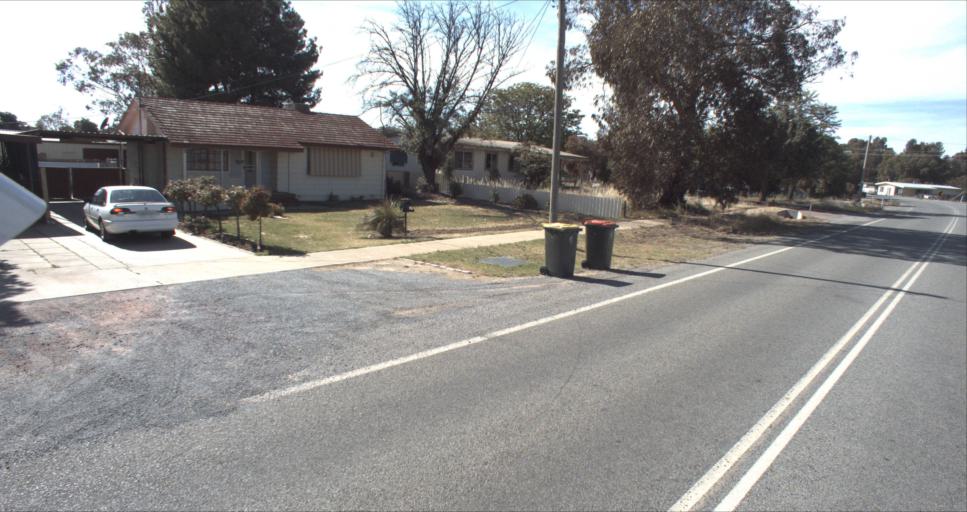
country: AU
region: New South Wales
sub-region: Leeton
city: Leeton
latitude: -34.6009
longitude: 146.4062
